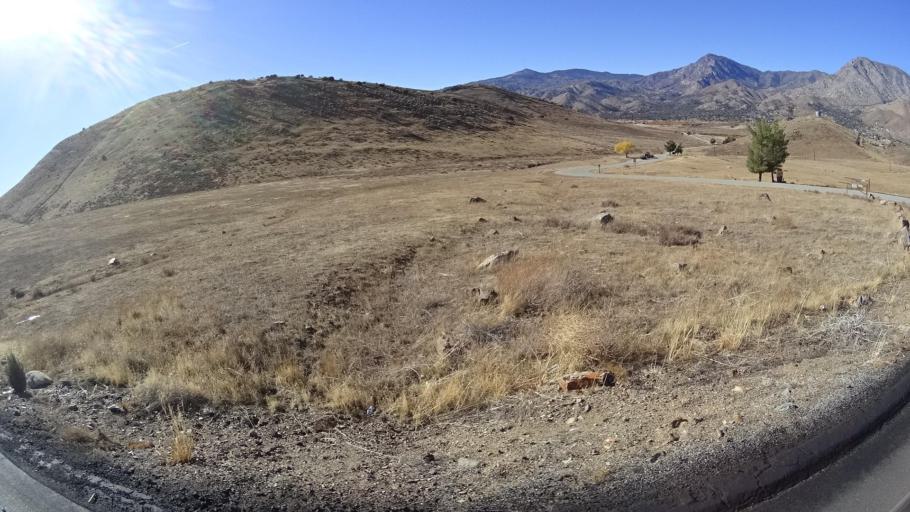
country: US
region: California
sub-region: Kern County
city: Wofford Heights
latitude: 35.6908
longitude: -118.4254
